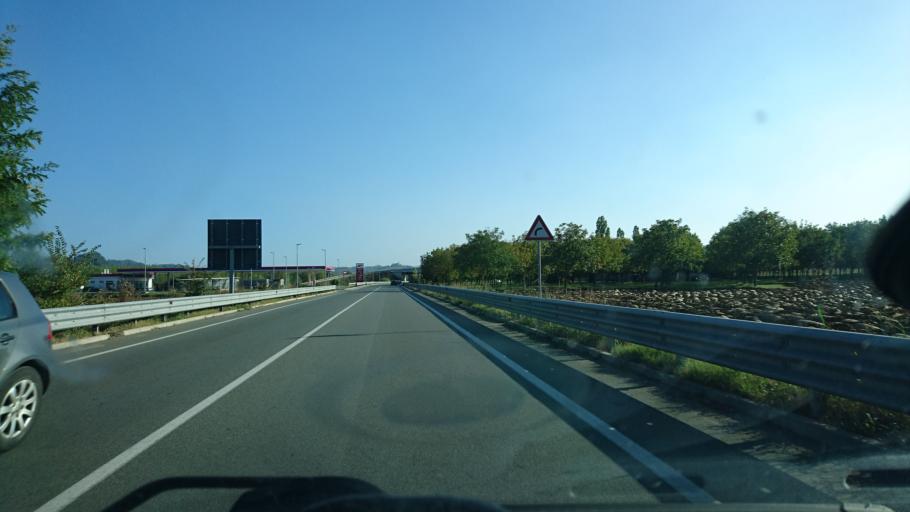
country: IT
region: Piedmont
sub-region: Provincia di Alessandria
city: Strevi
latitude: 44.7150
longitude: 8.5312
